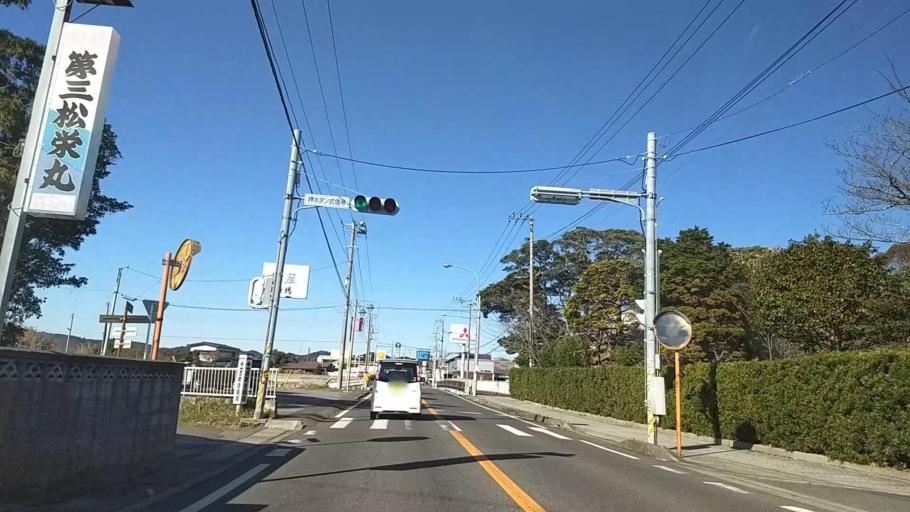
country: JP
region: Chiba
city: Ohara
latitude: 35.2556
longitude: 140.3946
